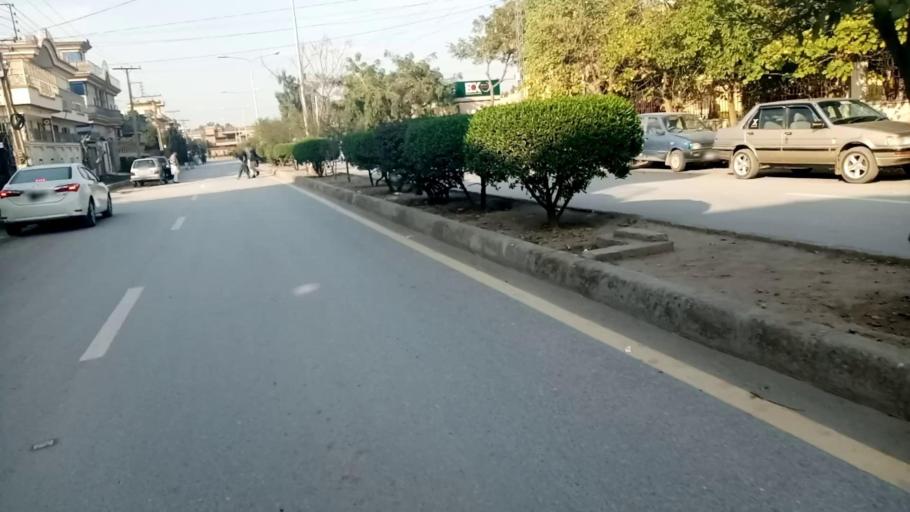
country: PK
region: Khyber Pakhtunkhwa
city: Peshawar
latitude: 33.9919
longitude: 71.4459
